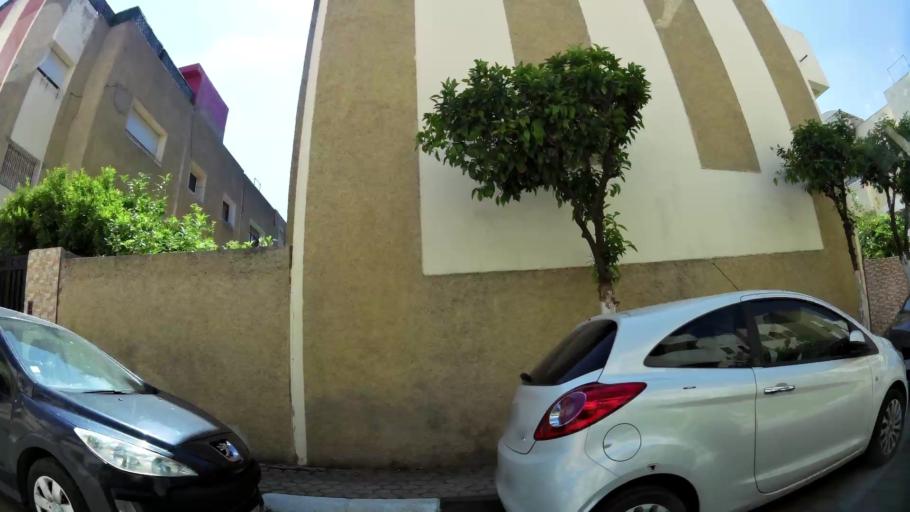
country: MA
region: Fes-Boulemane
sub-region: Fes
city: Fes
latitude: 34.0243
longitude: -5.0180
